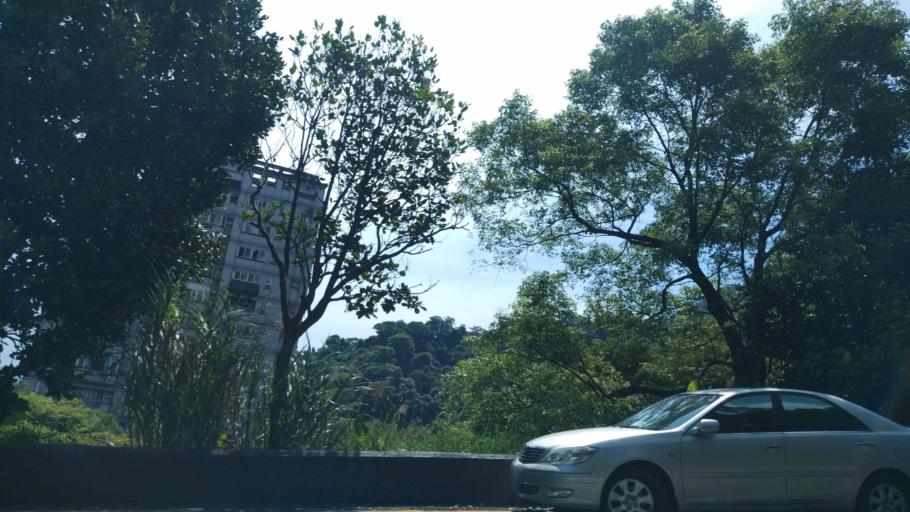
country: TW
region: Taipei
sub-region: Taipei
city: Banqiao
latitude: 24.9425
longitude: 121.5041
